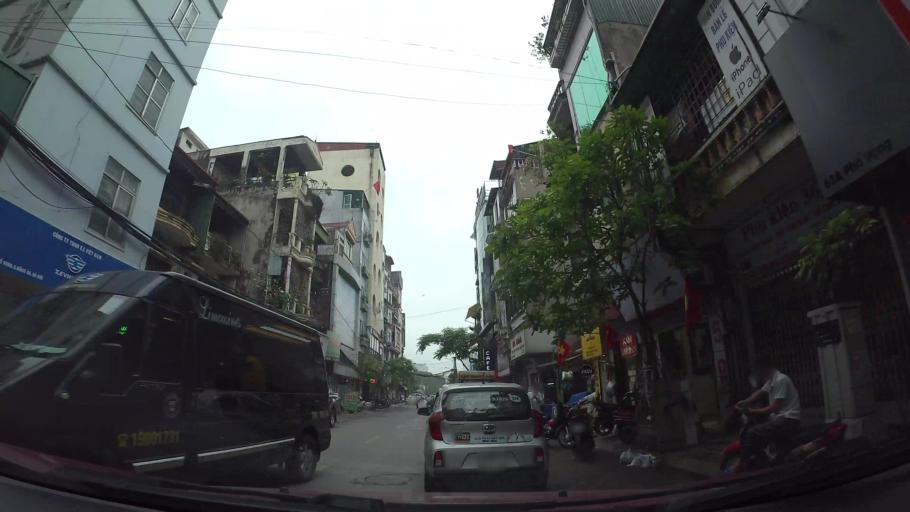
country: VN
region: Ha Noi
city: Hai BaTrung
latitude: 20.9990
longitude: 105.8419
